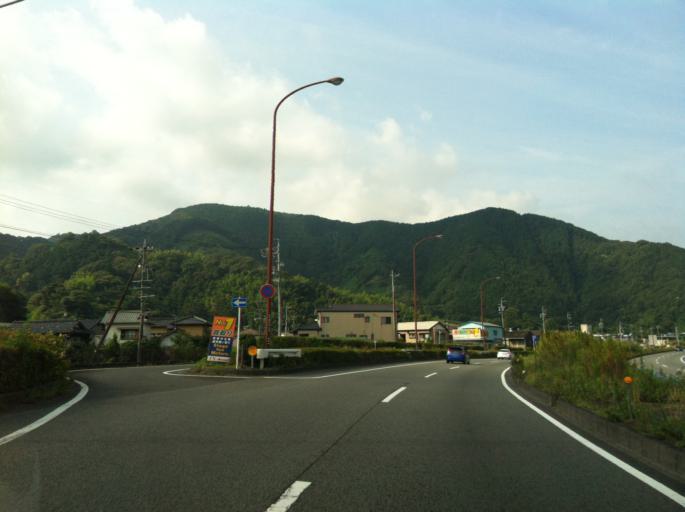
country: JP
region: Shizuoka
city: Shizuoka-shi
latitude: 34.9448
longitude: 138.3298
